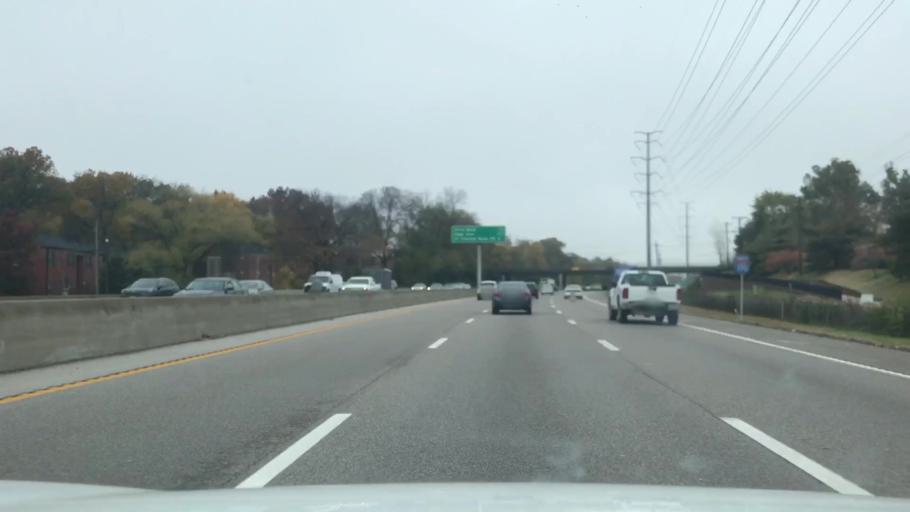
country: US
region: Missouri
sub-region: Saint Louis County
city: Olivette
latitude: 38.6657
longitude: -90.3602
